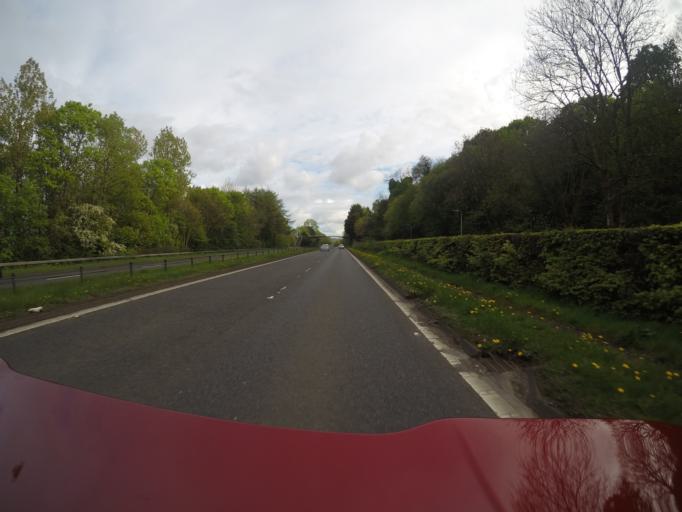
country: GB
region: Scotland
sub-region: West Dunbartonshire
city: Renton
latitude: 55.9706
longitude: -4.5877
